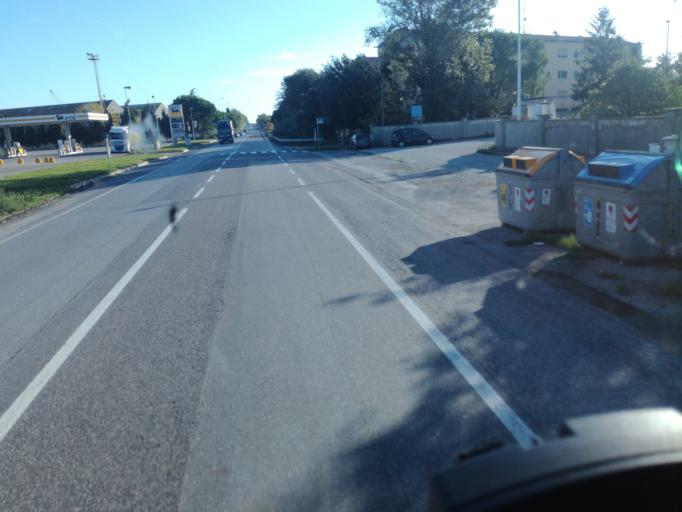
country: IT
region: Emilia-Romagna
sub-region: Provincia di Ravenna
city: Porto Fuori
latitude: 44.4337
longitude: 12.2415
